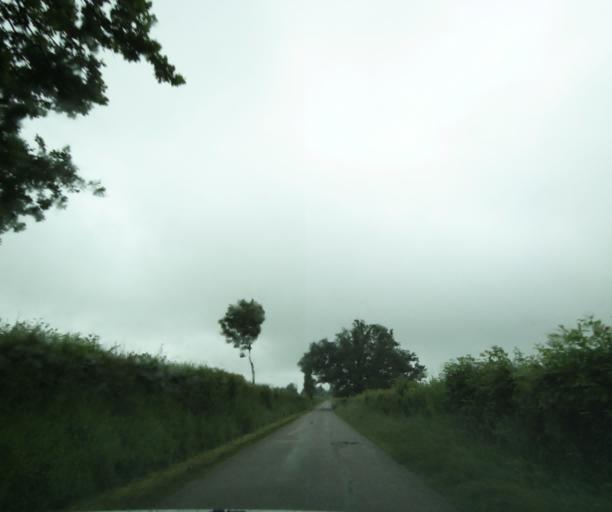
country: FR
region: Bourgogne
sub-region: Departement de Saone-et-Loire
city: Charolles
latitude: 46.3645
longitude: 4.2131
